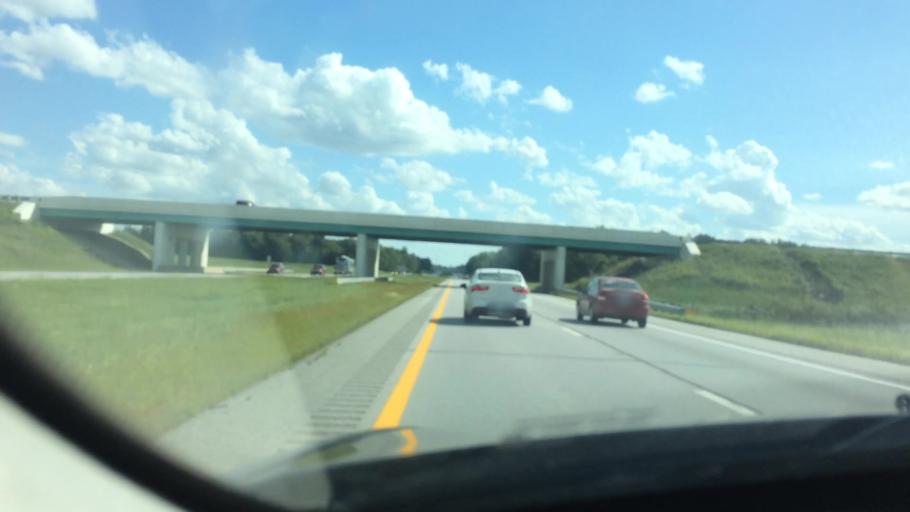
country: US
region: Ohio
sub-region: Shelby County
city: Botkins
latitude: 40.4404
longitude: -84.1694
